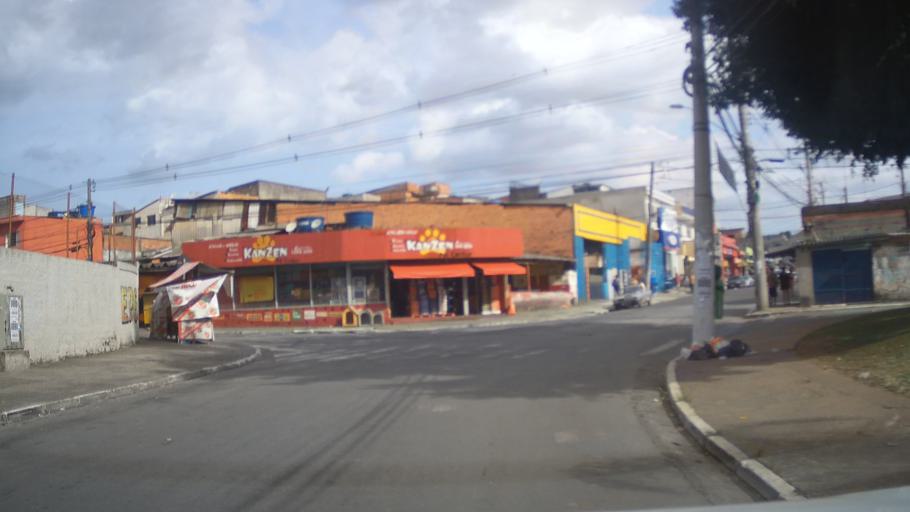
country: BR
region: Sao Paulo
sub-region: Guarulhos
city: Guarulhos
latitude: -23.4056
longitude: -46.4547
